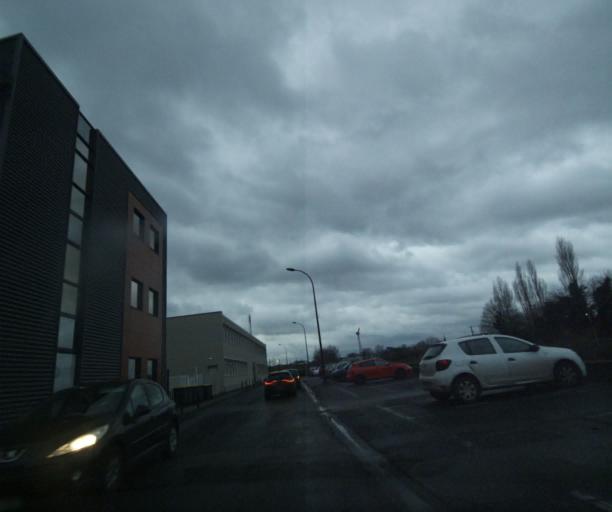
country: FR
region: Nord-Pas-de-Calais
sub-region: Departement du Nord
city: Anzin
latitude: 50.3694
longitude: 3.5213
